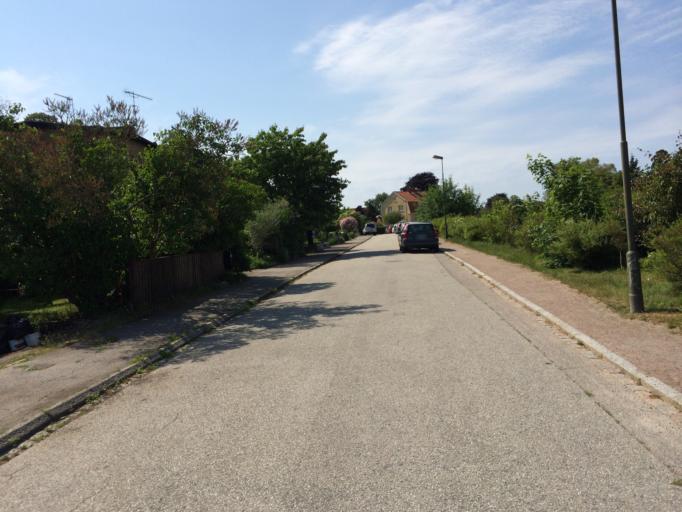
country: SE
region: Skane
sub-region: Malmo
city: Bunkeflostrand
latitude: 55.5757
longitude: 12.9482
